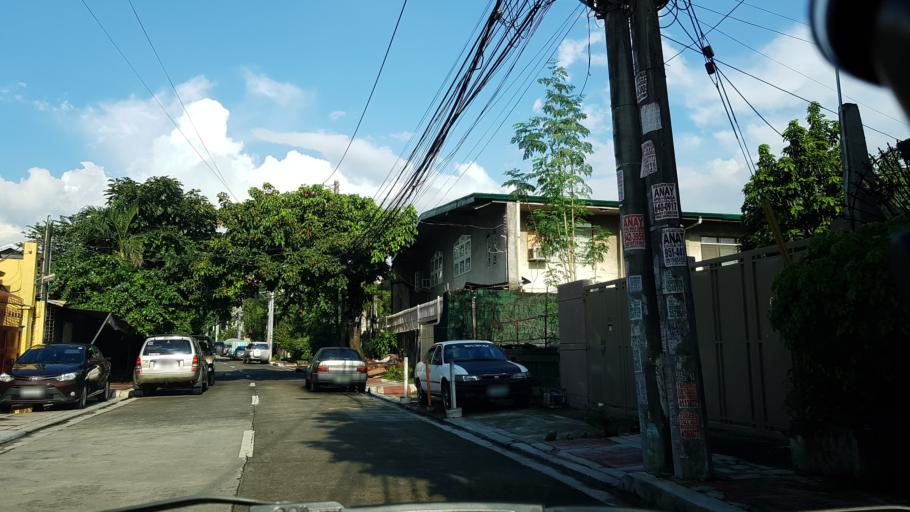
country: PH
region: Metro Manila
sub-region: Quezon City
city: Quezon City
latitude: 14.6432
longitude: 121.0503
